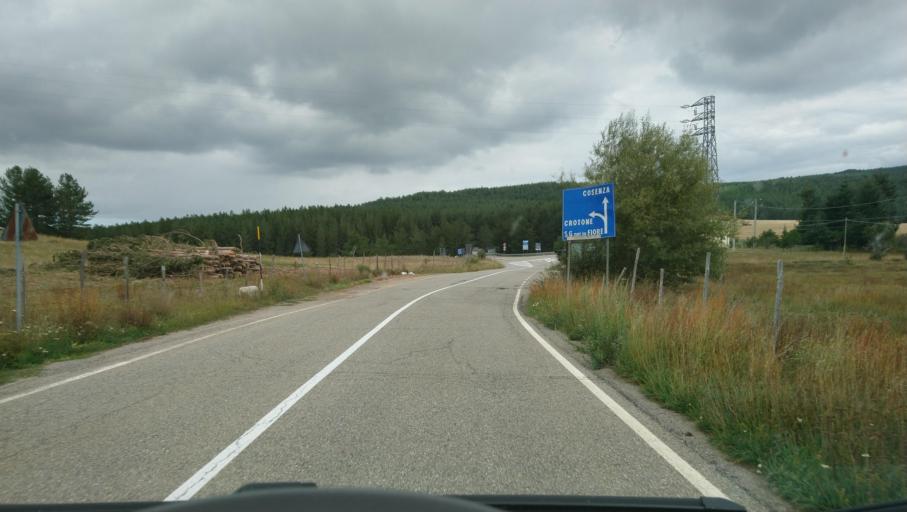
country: IT
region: Calabria
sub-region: Provincia di Cosenza
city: Longobucco
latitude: 39.3150
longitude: 16.5449
